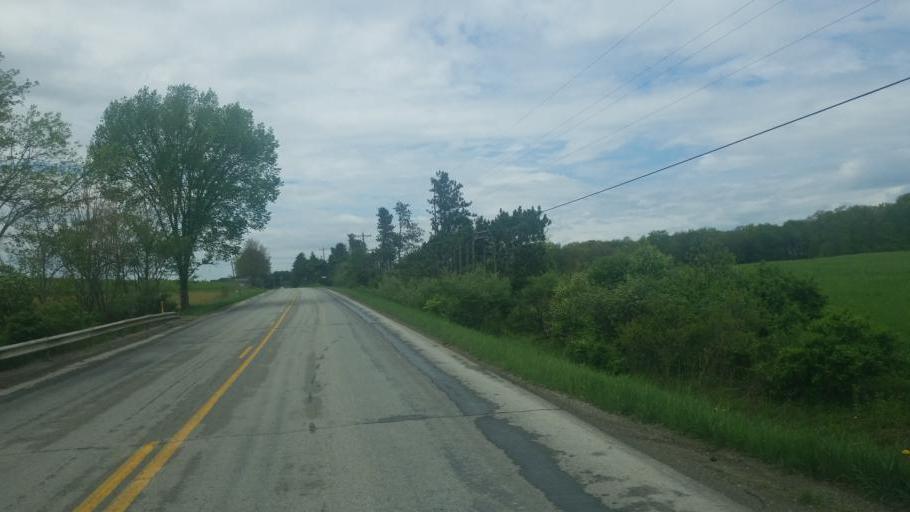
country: US
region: Pennsylvania
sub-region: Clarion County
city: Marianne
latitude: 41.3722
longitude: -79.4009
